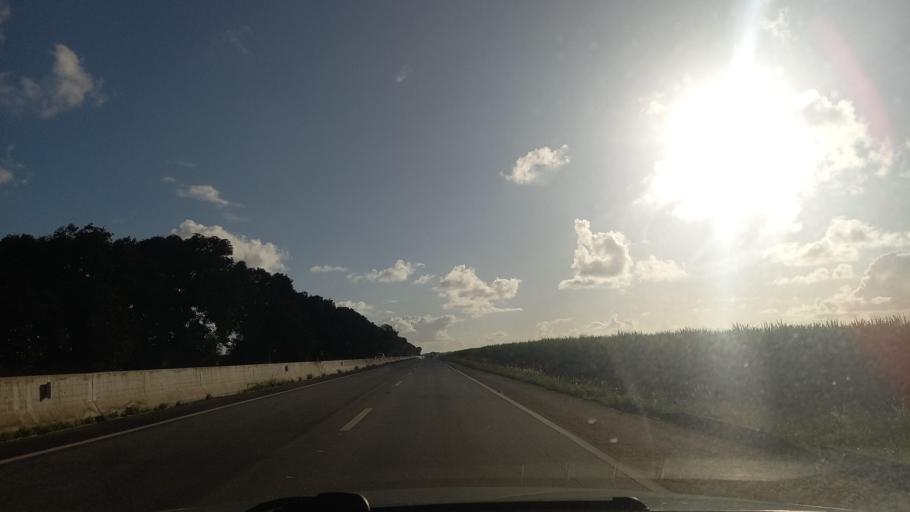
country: BR
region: Alagoas
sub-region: Sao Miguel Dos Campos
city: Sao Miguel dos Campos
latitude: -9.8005
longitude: -36.1715
